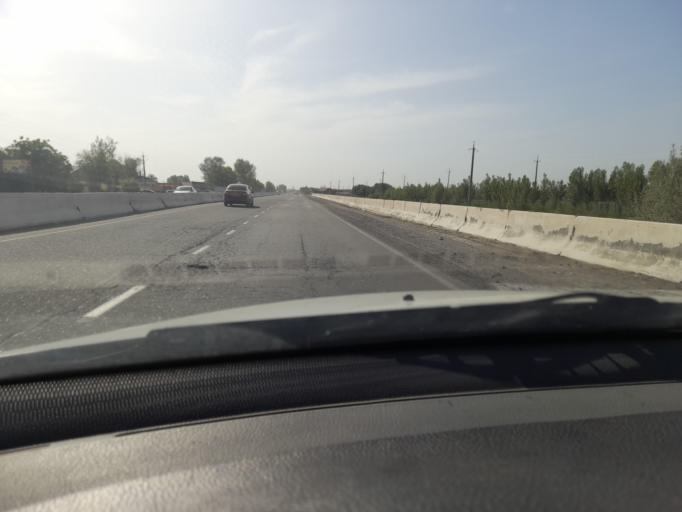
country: UZ
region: Samarqand
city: Kattaqo'rg'on
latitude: 39.9192
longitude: 66.2984
